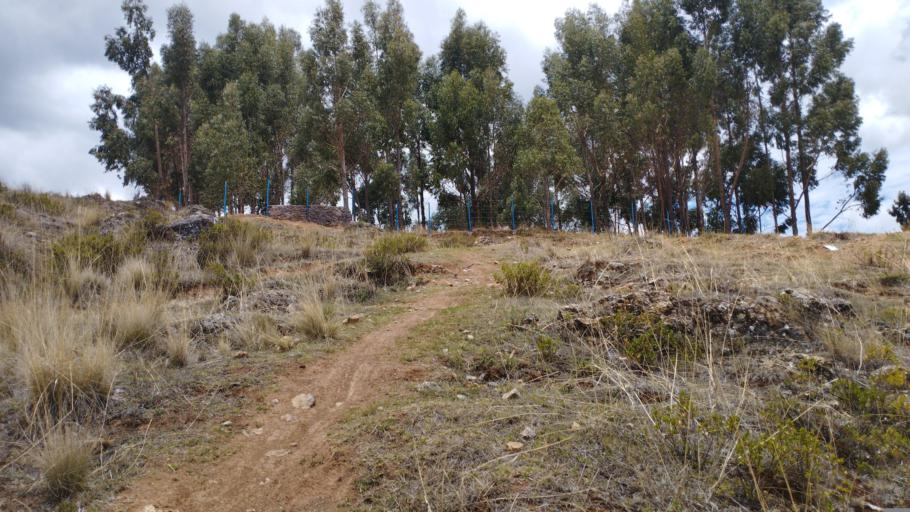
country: PE
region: Cusco
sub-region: Provincia de Cusco
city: Cusco
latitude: -13.5147
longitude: -71.9420
